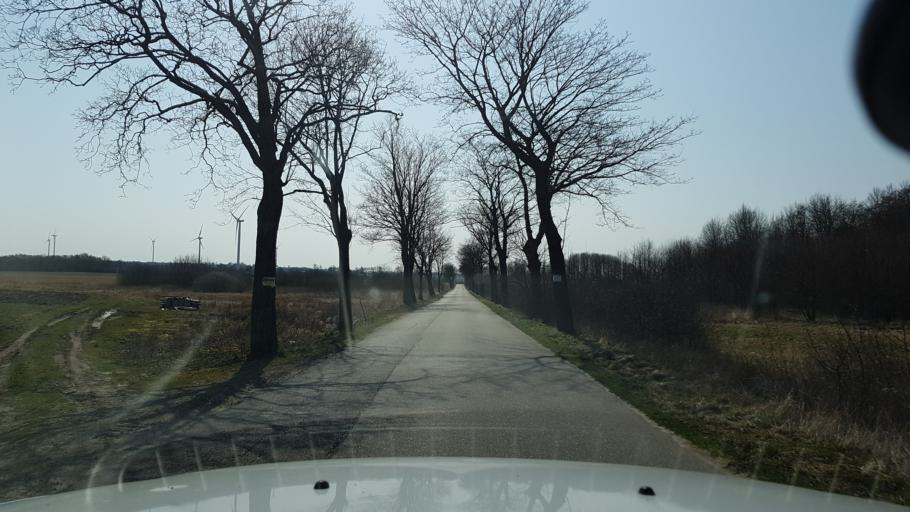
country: PL
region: West Pomeranian Voivodeship
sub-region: Powiat slawienski
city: Darlowo
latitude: 54.5018
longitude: 16.5053
